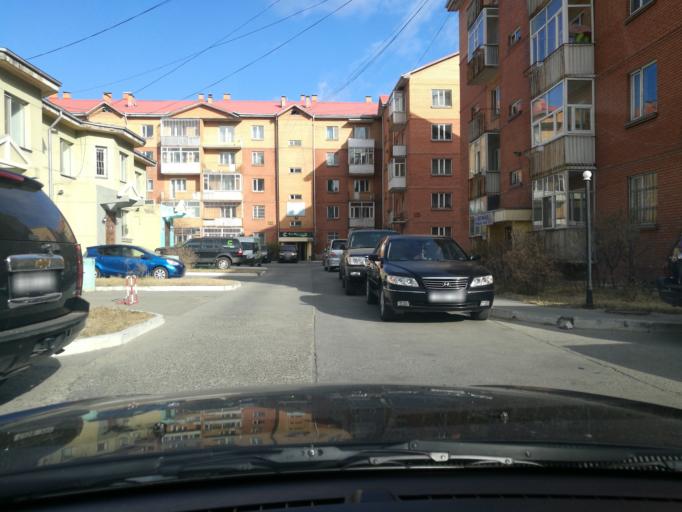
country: MN
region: Ulaanbaatar
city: Ulaanbaatar
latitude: 47.9052
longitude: 106.9272
